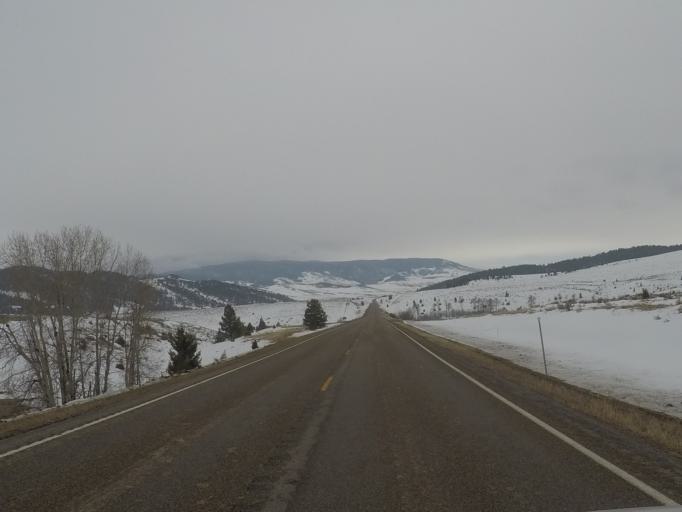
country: US
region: Montana
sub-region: Meagher County
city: White Sulphur Springs
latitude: 46.6279
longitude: -110.8487
